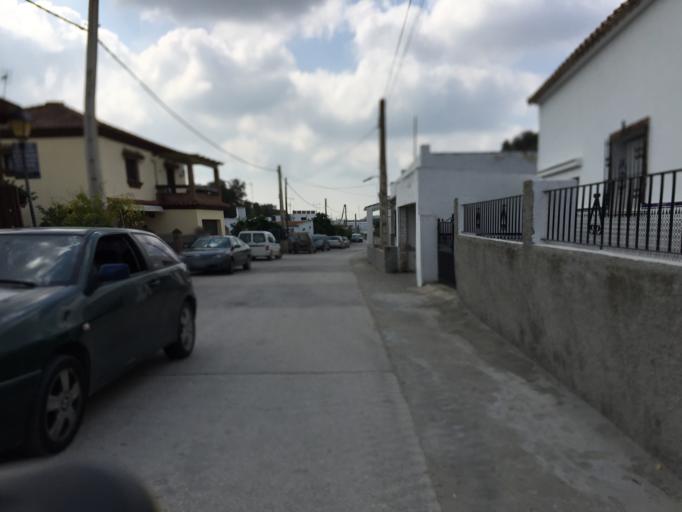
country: ES
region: Andalusia
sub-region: Provincia de Cadiz
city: Benalup-Casas Viejas
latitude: 36.3176
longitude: -5.8847
